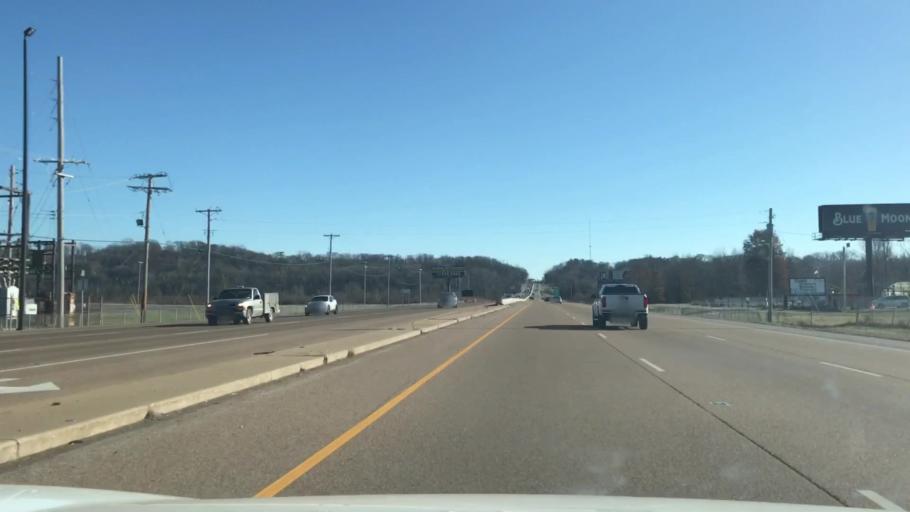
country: US
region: Illinois
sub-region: Saint Clair County
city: Alorton
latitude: 38.5738
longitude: -90.0983
